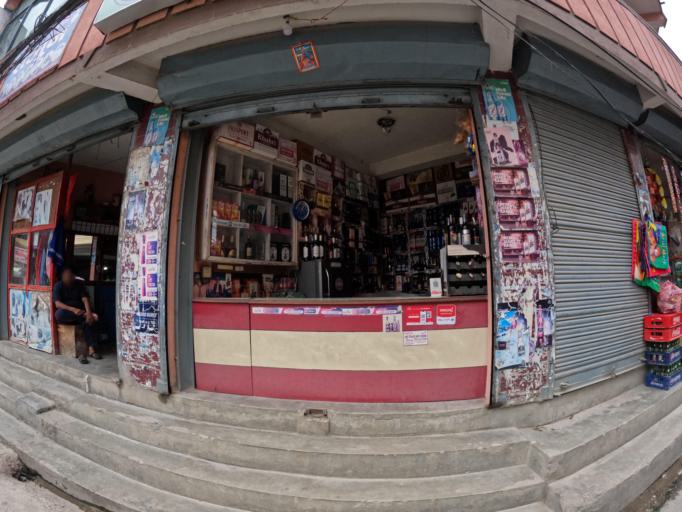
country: NP
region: Central Region
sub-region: Bagmati Zone
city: Kathmandu
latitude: 27.7361
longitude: 85.3119
